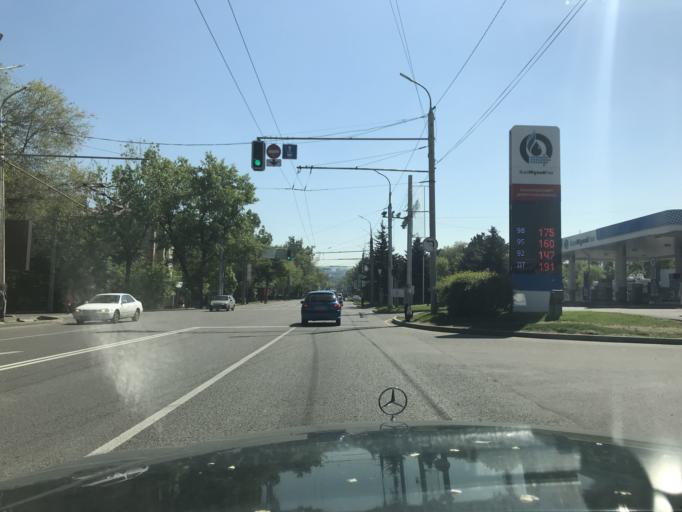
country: KZ
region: Almaty Qalasy
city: Almaty
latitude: 43.2261
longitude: 76.9098
